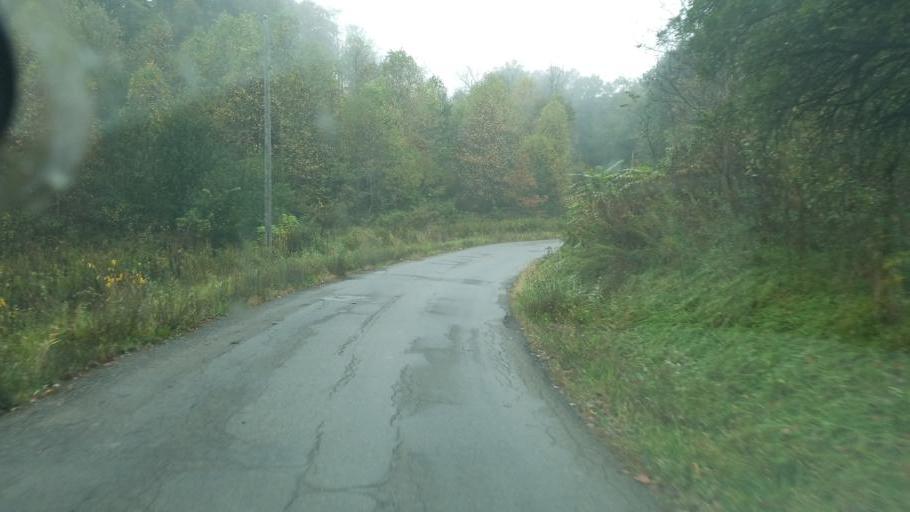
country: US
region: Ohio
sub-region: Harrison County
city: Cadiz
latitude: 40.3870
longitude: -81.1068
